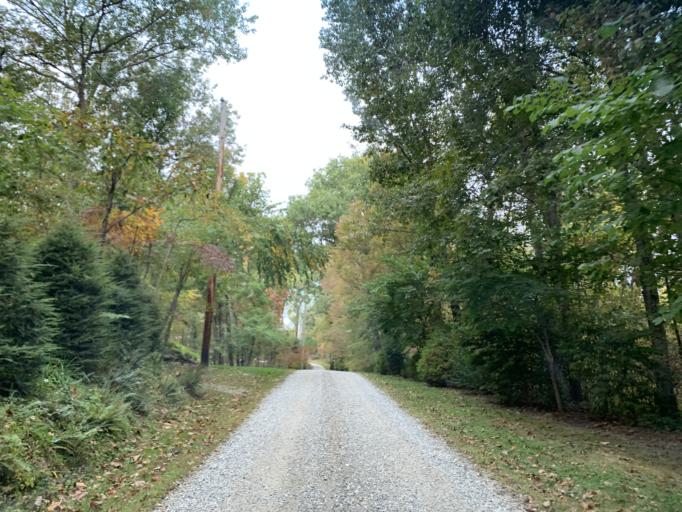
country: US
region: Pennsylvania
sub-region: York County
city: Susquehanna Trails
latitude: 39.8004
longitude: -76.4309
